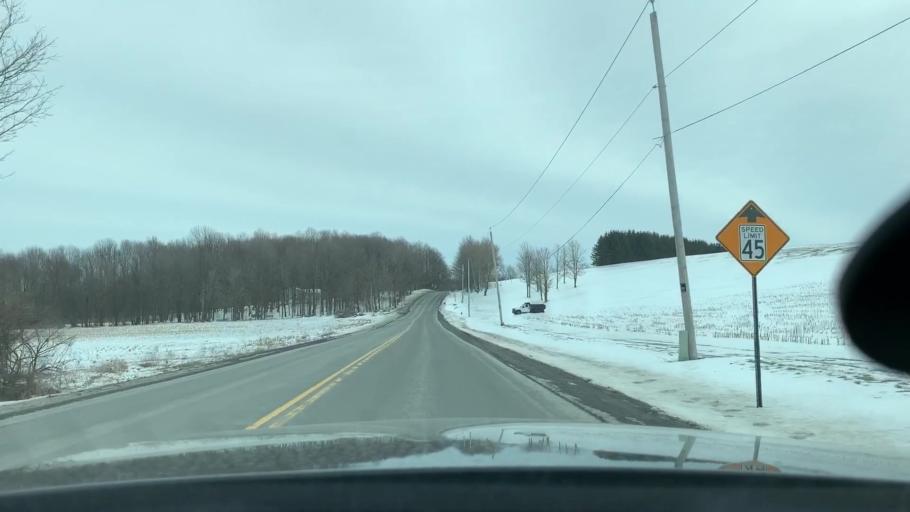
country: US
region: New York
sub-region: Oneida County
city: Washington Mills
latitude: 43.0448
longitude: -75.2202
